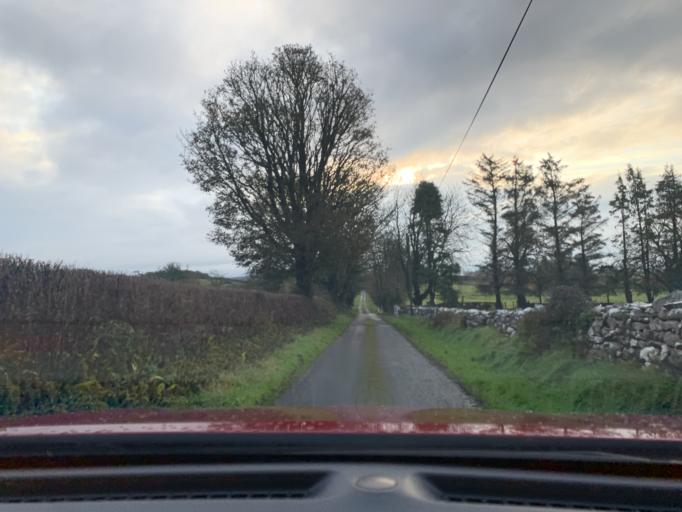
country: IE
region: Connaught
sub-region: Sligo
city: Ballymote
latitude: 54.0343
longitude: -8.5364
